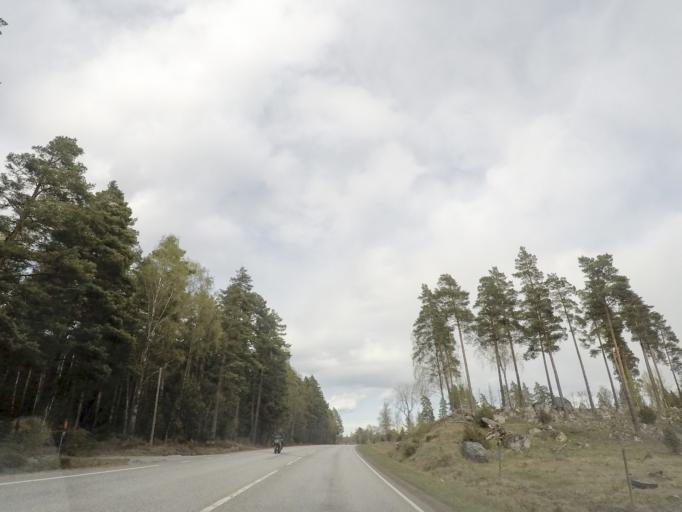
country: SE
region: Vaestmanland
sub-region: Kungsors Kommun
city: Kungsoer
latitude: 59.2939
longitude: 16.1990
